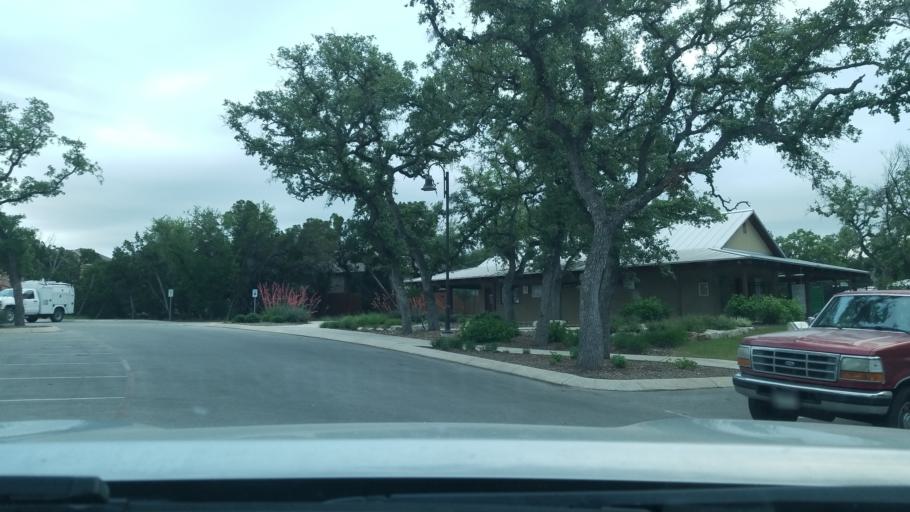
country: US
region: Texas
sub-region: Bexar County
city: Timberwood Park
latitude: 29.7176
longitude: -98.4556
